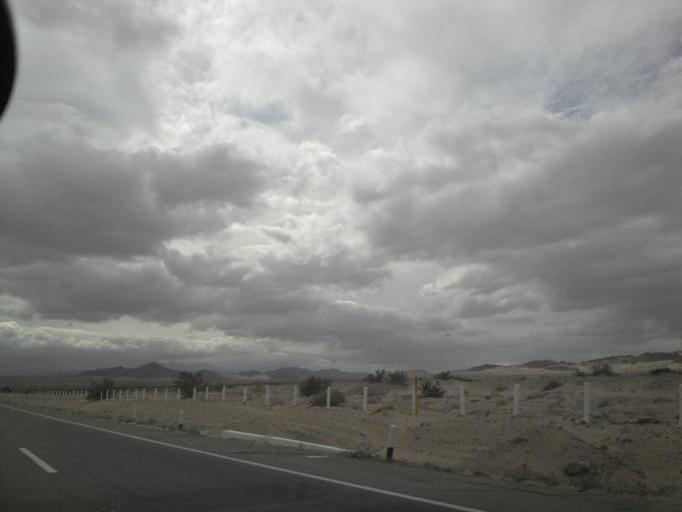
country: MX
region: Baja California
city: Progreso
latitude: 32.5752
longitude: -115.7584
